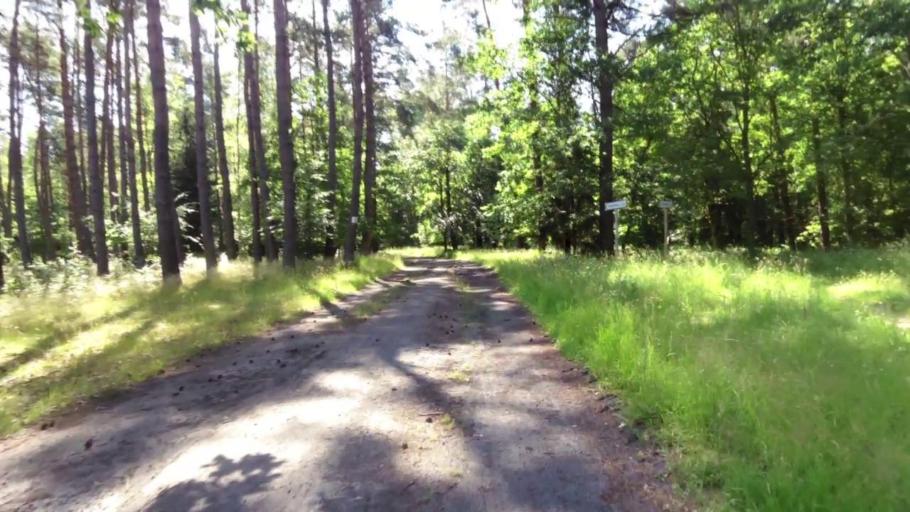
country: PL
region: West Pomeranian Voivodeship
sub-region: Powiat swidwinski
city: Polczyn-Zdroj
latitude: 53.8426
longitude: 16.1482
